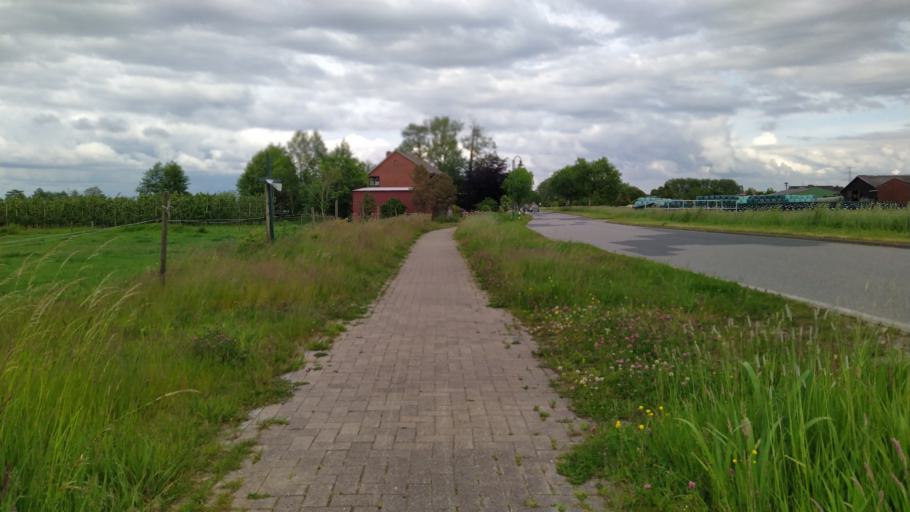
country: DE
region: Lower Saxony
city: Neu Wulmstorf
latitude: 53.4906
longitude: 9.7513
